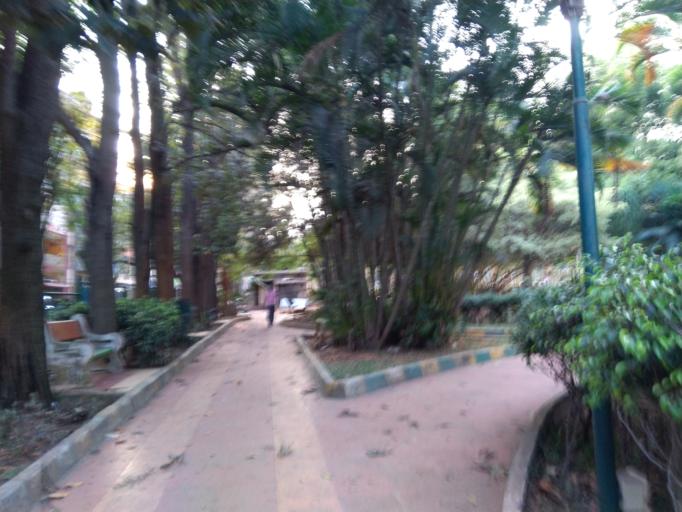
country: IN
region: Karnataka
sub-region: Bangalore Urban
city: Bangalore
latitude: 12.9104
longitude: 77.6111
